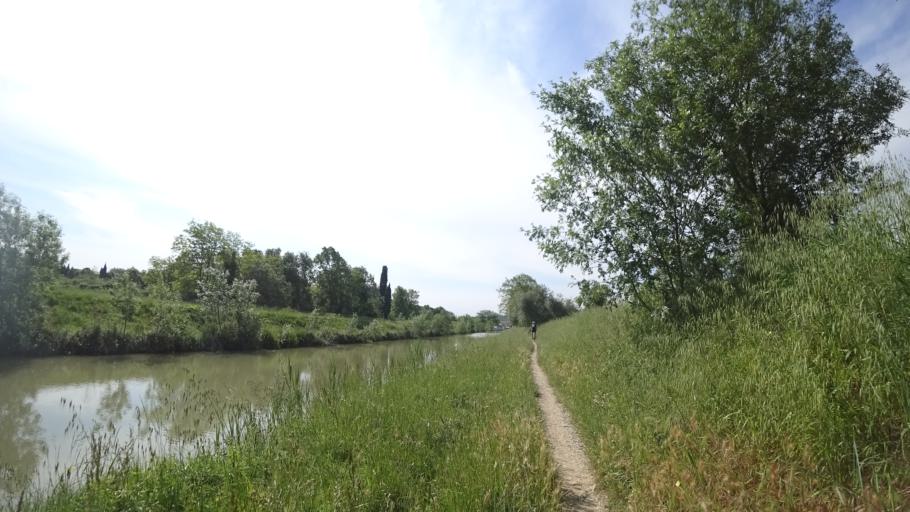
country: FR
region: Languedoc-Roussillon
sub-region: Departement de l'Aude
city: Lezignan-Corbieres
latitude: 43.2453
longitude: 2.7623
